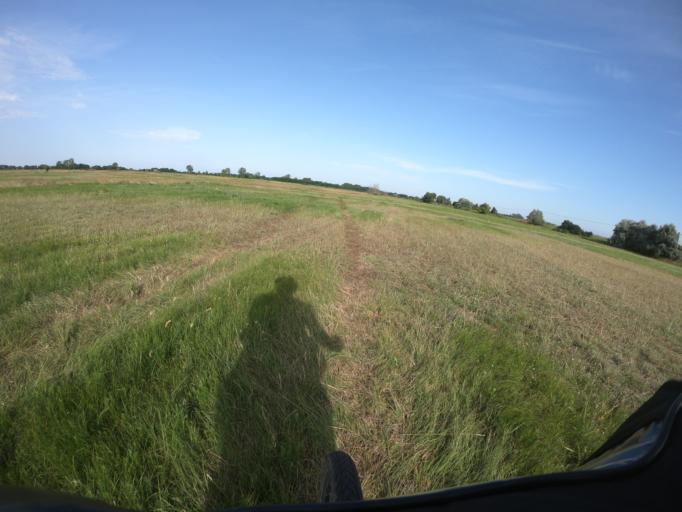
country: HU
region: Hajdu-Bihar
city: Tiszacsege
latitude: 47.6138
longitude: 21.0223
